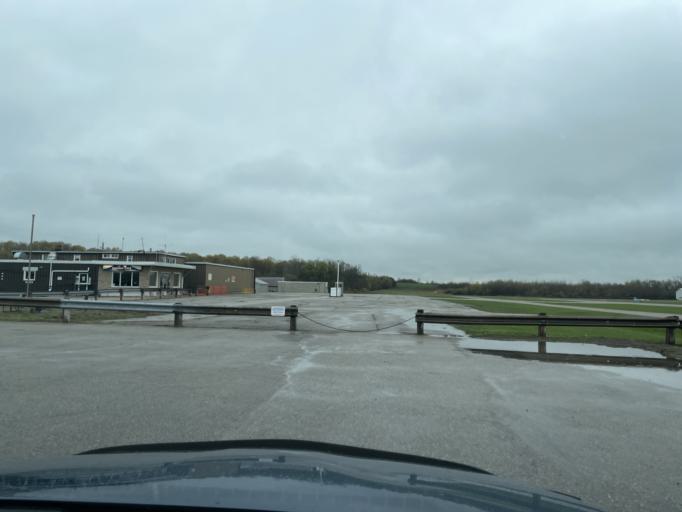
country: CA
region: Ontario
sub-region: Wellington County
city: Guelph
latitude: 43.5638
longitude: -80.1958
